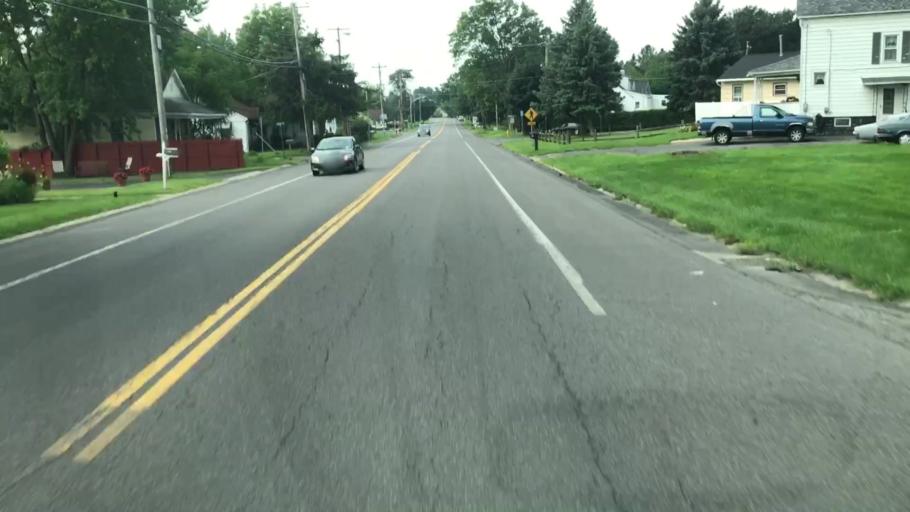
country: US
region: New York
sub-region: Onondaga County
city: Galeville
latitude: 43.0867
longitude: -76.1750
